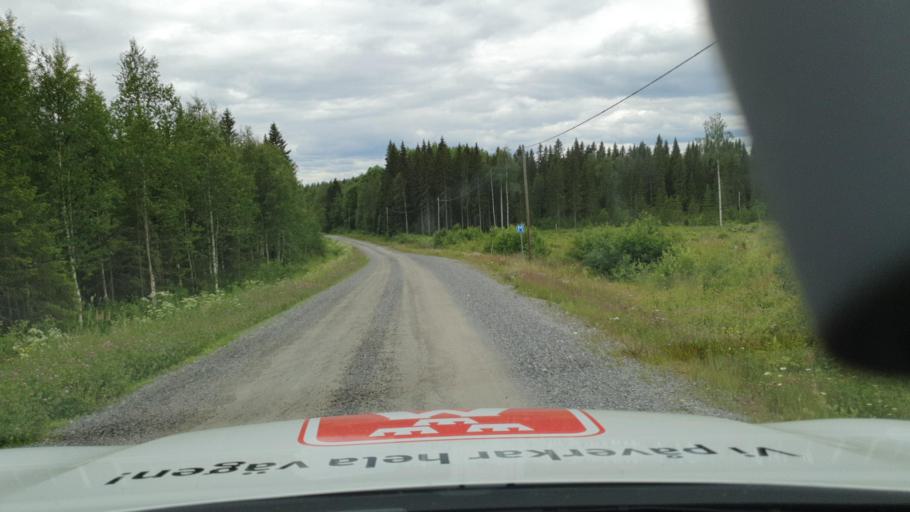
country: SE
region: Vaesterbotten
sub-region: Bjurholms Kommun
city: Bjurholm
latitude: 63.7673
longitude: 19.3220
